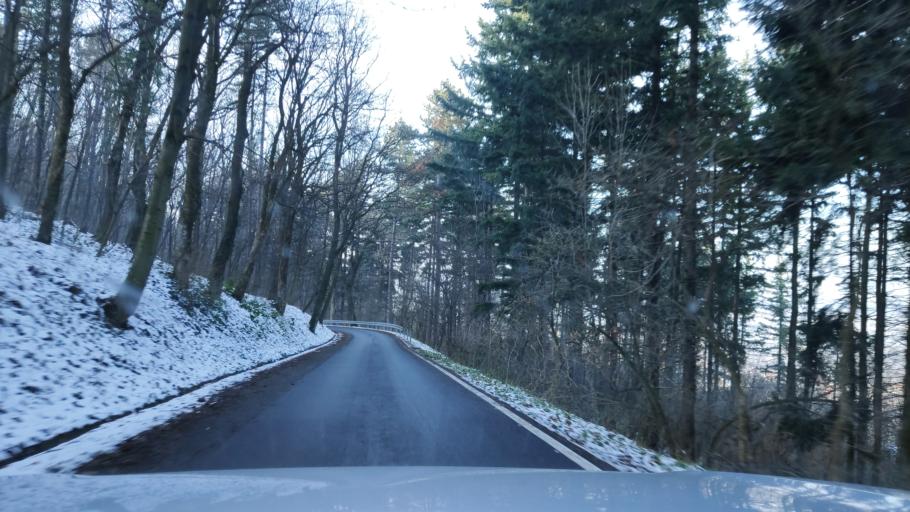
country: RS
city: Rusanj
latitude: 44.6988
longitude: 20.5195
